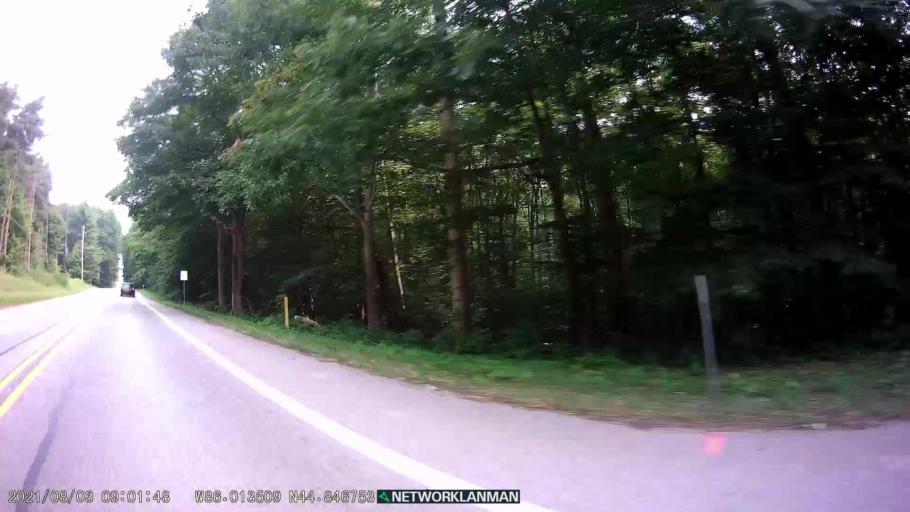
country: US
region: Michigan
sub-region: Benzie County
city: Beulah
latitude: 44.8464
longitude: -86.0137
